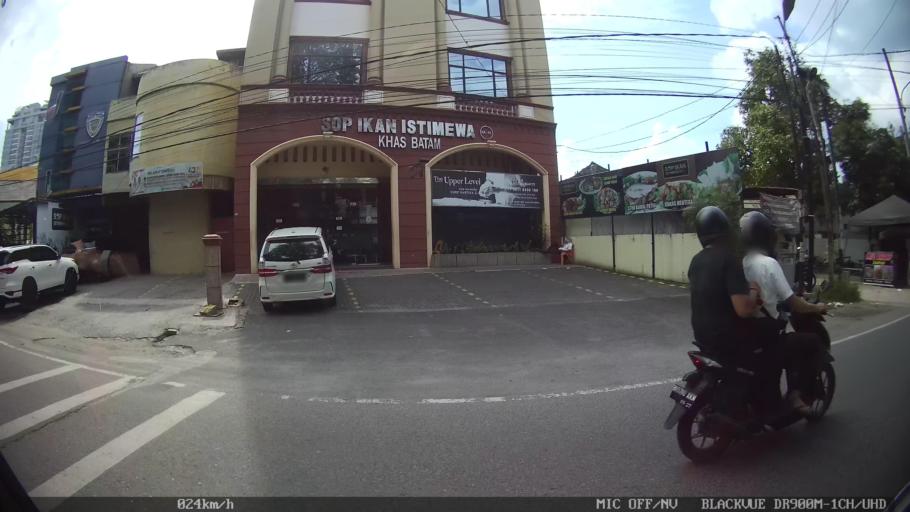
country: ID
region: North Sumatra
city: Medan
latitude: 3.5865
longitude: 98.6700
